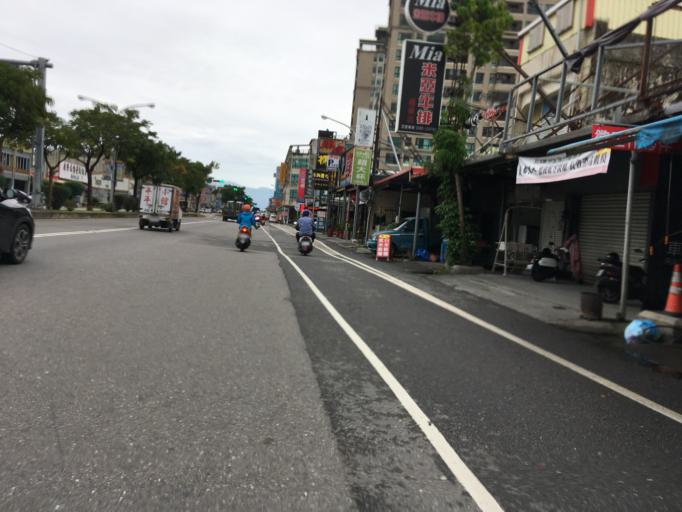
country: TW
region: Taiwan
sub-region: Yilan
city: Yilan
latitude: 24.6892
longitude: 121.7705
